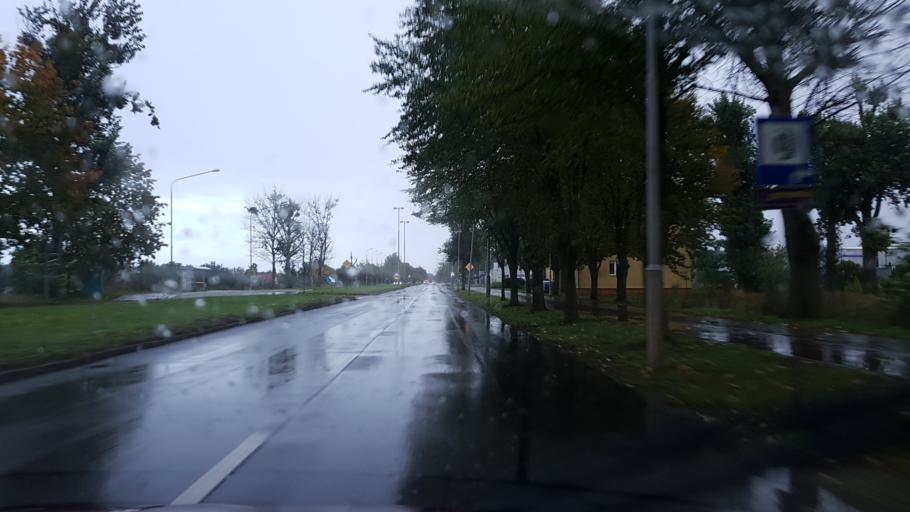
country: PL
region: Greater Poland Voivodeship
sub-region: Powiat pilski
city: Pila
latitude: 53.1540
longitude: 16.6949
